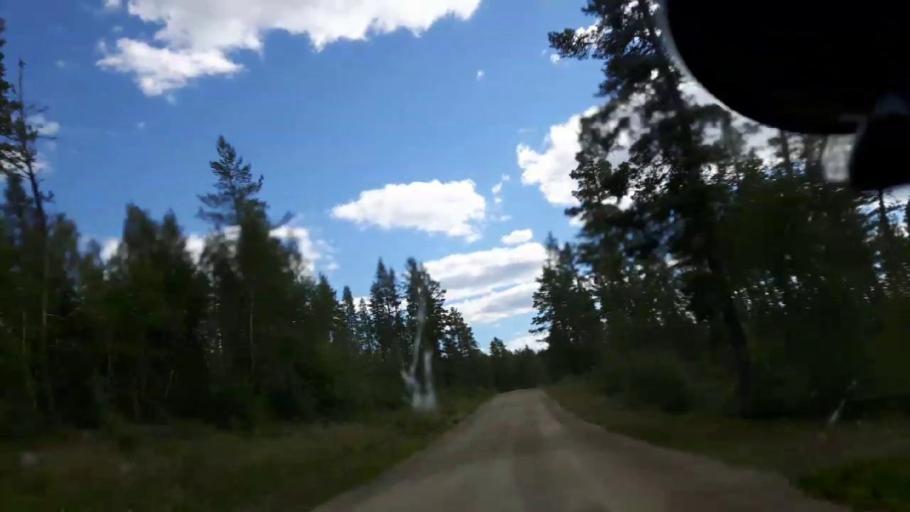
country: SE
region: Vaesternorrland
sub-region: Ange Kommun
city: Ange
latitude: 62.7344
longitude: 15.6452
